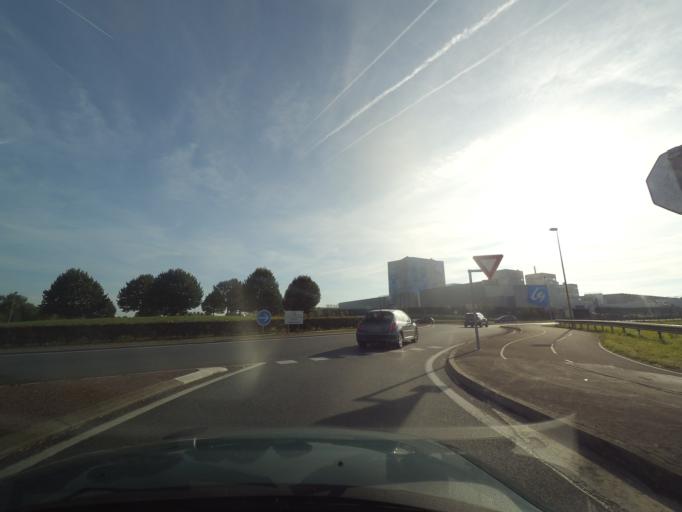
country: FR
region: Pays de la Loire
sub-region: Departement de la Vendee
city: Montaigu
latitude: 46.9644
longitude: -1.3077
